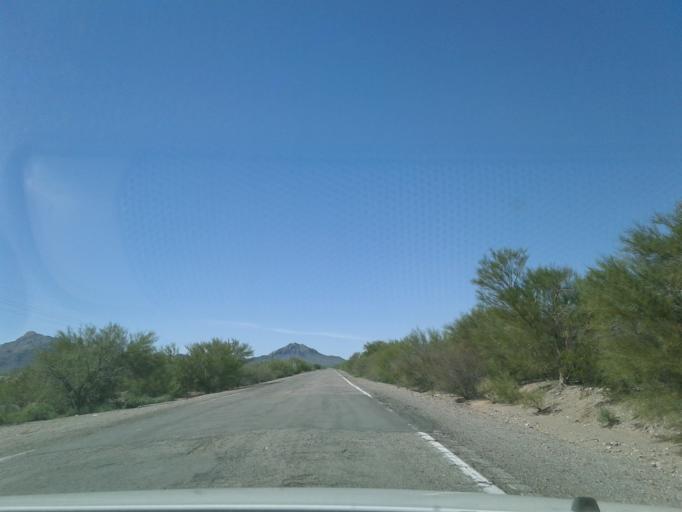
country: US
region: Arizona
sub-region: Pima County
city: Avra Valley
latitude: 32.3711
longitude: -111.4171
